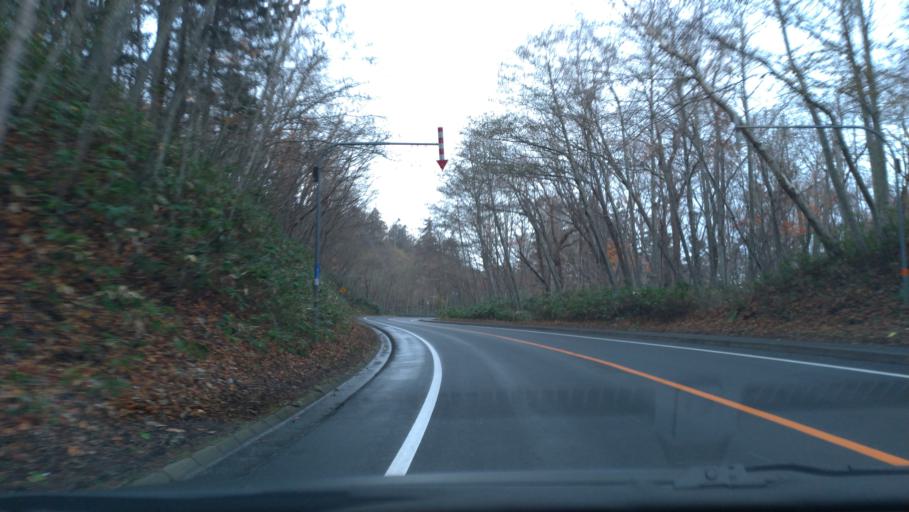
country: JP
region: Hokkaido
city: Shiraoi
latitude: 42.7354
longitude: 141.3717
